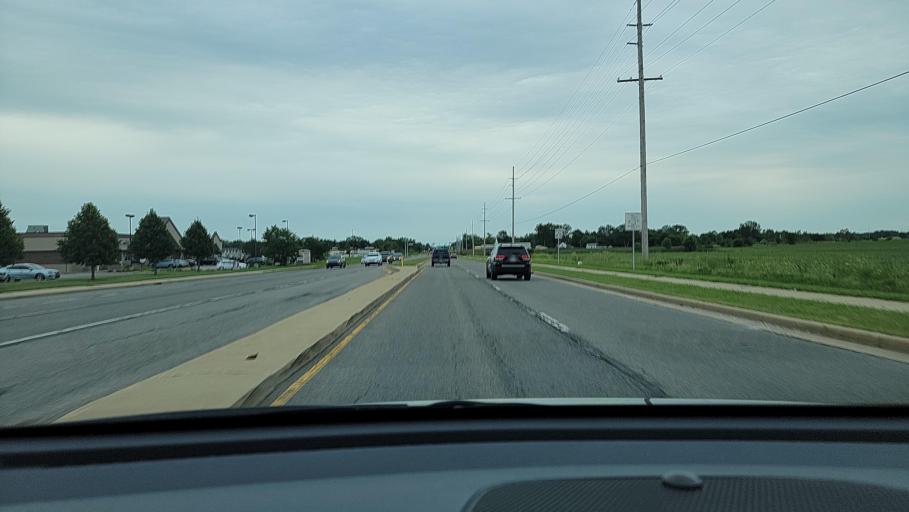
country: US
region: Indiana
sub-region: Porter County
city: South Haven
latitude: 41.5505
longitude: -87.1625
